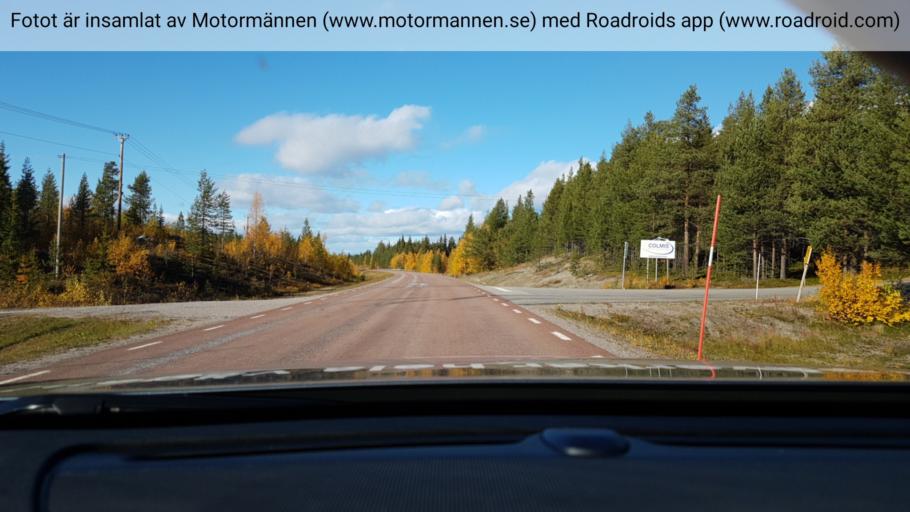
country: SE
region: Norrbotten
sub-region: Arjeplogs Kommun
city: Arjeplog
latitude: 66.0506
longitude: 18.0214
